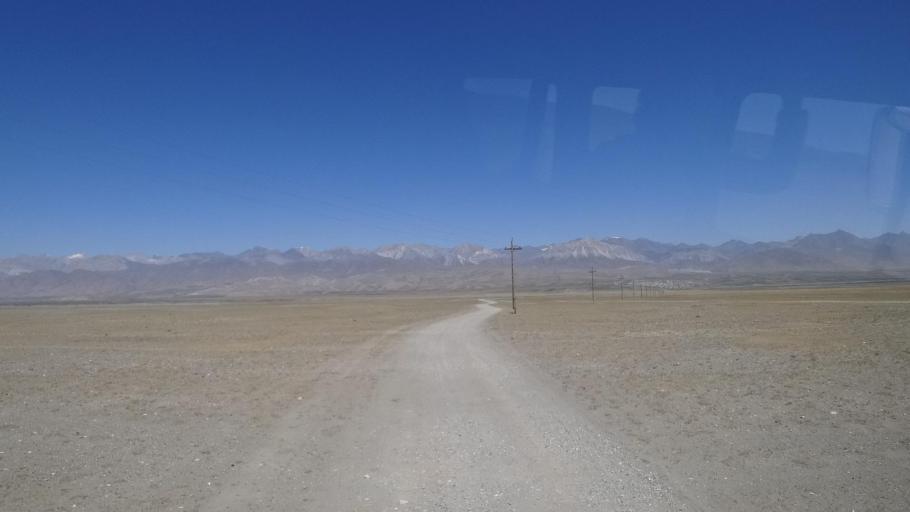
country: KG
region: Osh
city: Gul'cha
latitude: 39.6107
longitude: 72.8752
